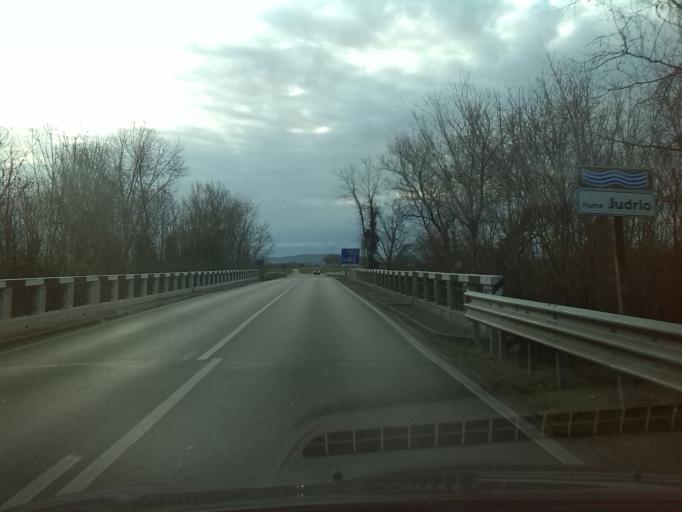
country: IT
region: Friuli Venezia Giulia
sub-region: Provincia di Udine
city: San Giovanni al Natisone
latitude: 45.9538
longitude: 13.4312
